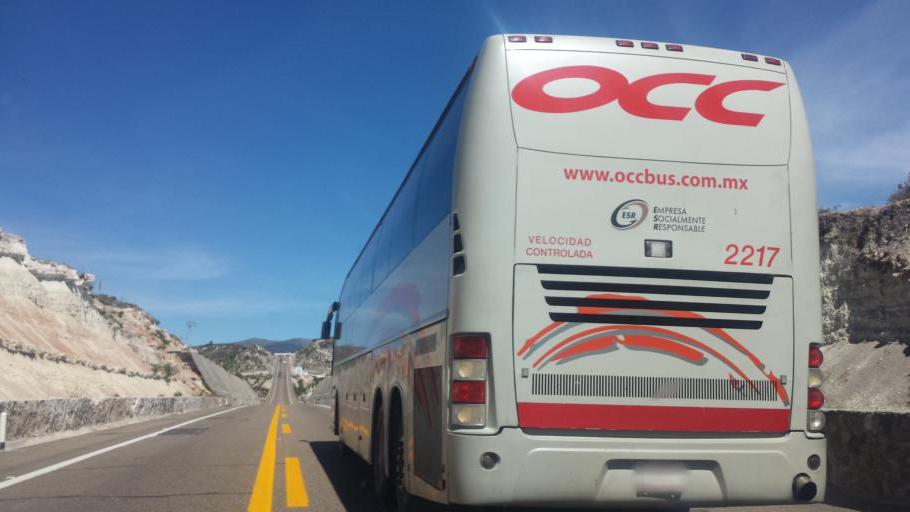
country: MX
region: Oaxaca
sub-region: Villa Tejupam de la Union
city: Villa Tejupam de la Union
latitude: 17.9057
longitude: -97.3656
